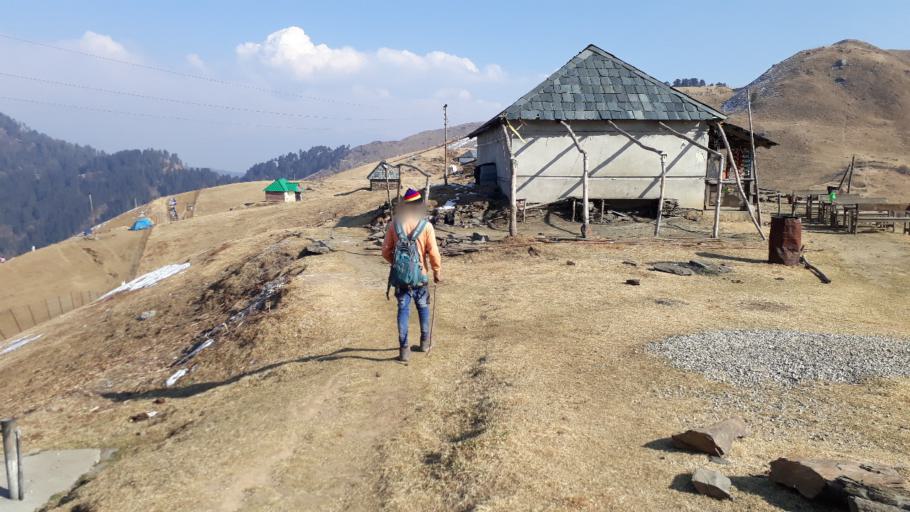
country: IN
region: Himachal Pradesh
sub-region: Mandi
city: Pandoh
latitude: 31.7559
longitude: 77.1001
